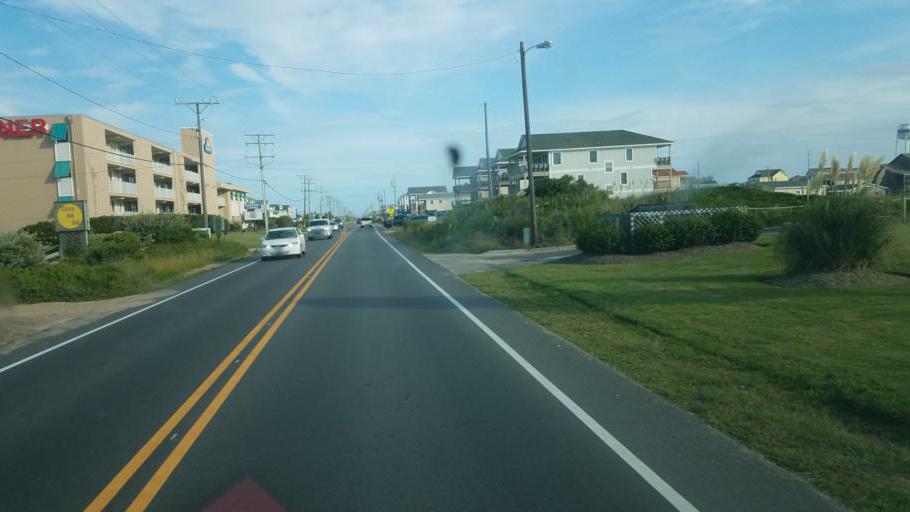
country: US
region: North Carolina
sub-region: Dare County
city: Kill Devil Hills
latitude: 36.0357
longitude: -75.6703
